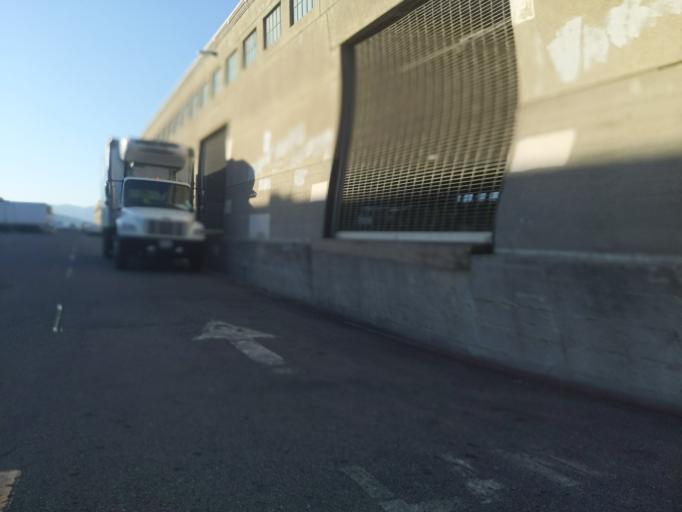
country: US
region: California
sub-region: San Francisco County
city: San Francisco
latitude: 37.8095
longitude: -122.4168
